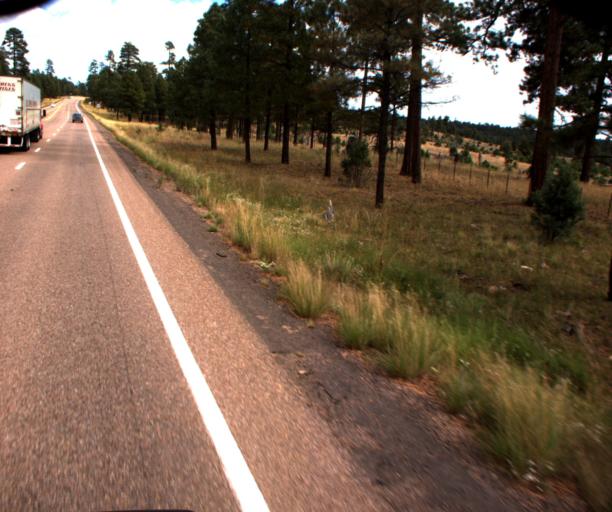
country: US
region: Arizona
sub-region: Navajo County
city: Heber-Overgaard
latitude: 34.3624
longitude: -110.6922
